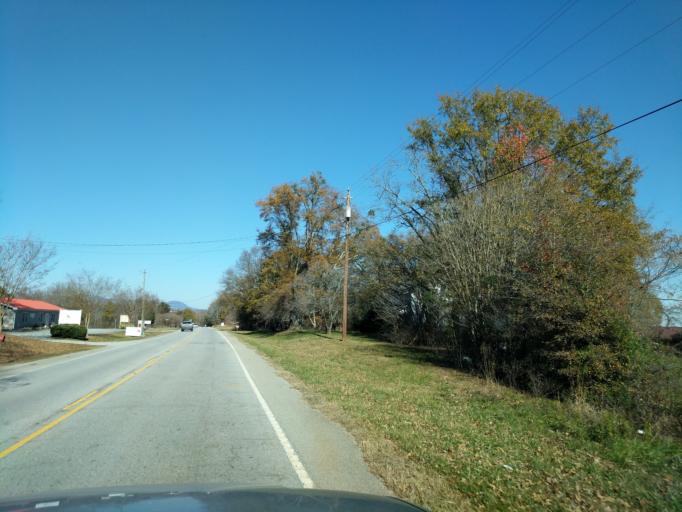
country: US
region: South Carolina
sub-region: Spartanburg County
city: Landrum
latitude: 35.1009
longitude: -82.2261
